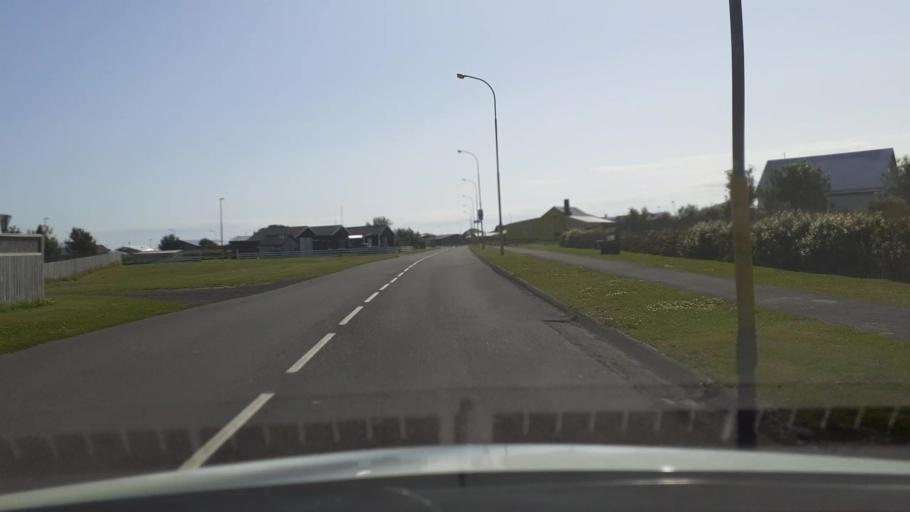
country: IS
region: South
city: Selfoss
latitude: 63.8361
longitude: -21.0613
